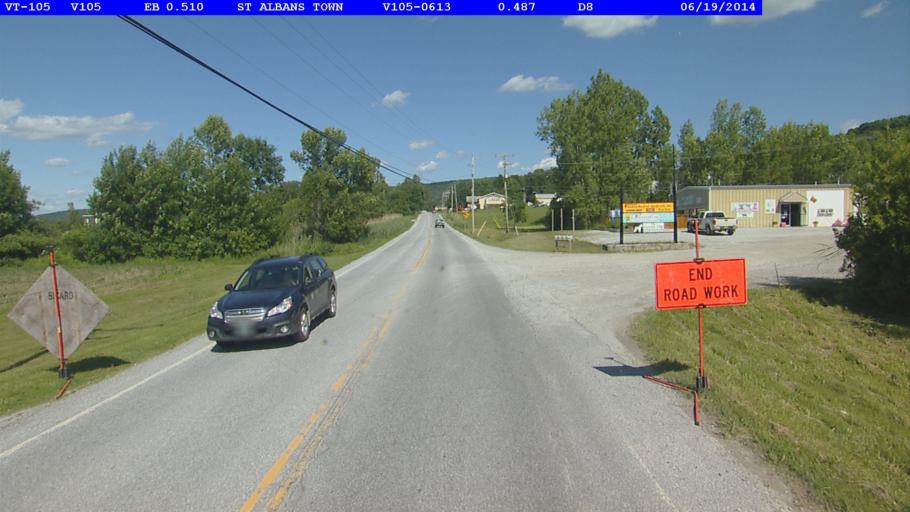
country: US
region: Vermont
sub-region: Franklin County
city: Saint Albans
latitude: 44.8271
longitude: -73.0730
